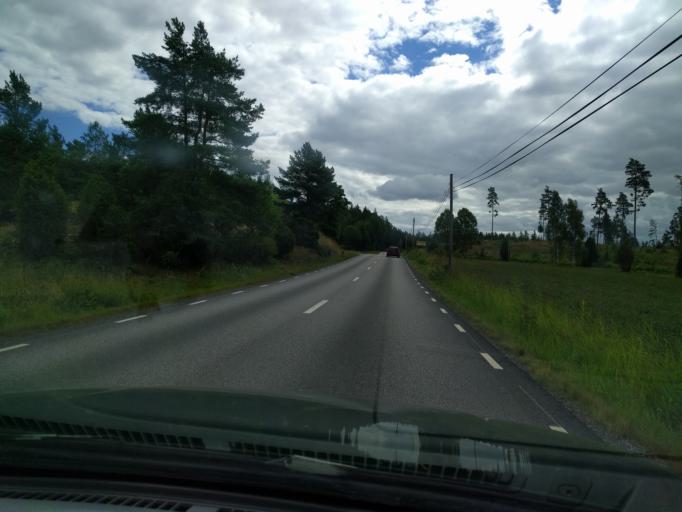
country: SE
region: Soedermanland
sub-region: Nykopings Kommun
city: Svalsta
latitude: 58.5263
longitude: 16.7636
